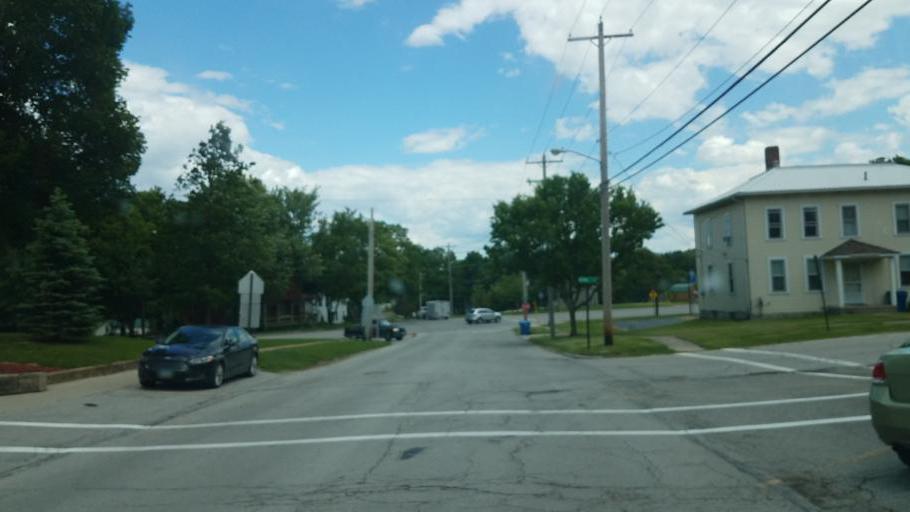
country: US
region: Ohio
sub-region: Huron County
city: Monroeville
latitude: 41.2454
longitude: -82.6970
